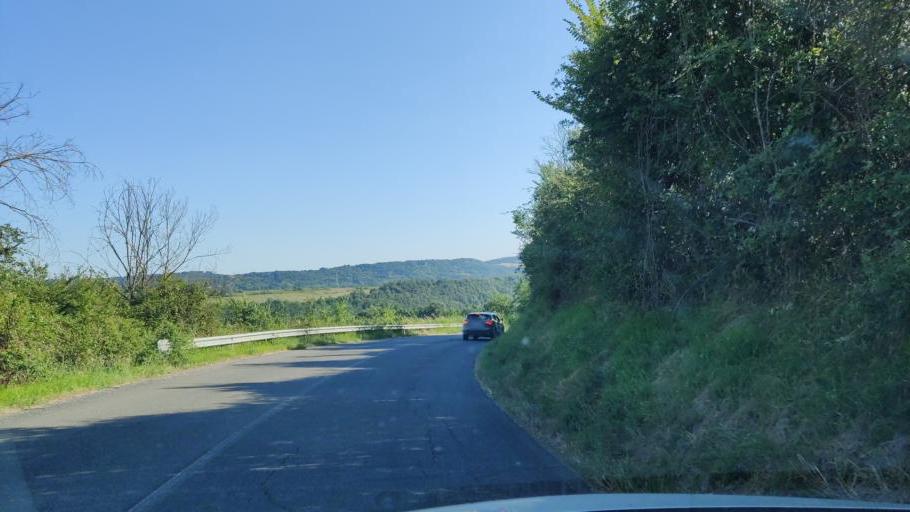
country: IT
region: Umbria
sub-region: Provincia di Terni
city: Penna in Teverina
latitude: 42.4857
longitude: 12.3693
